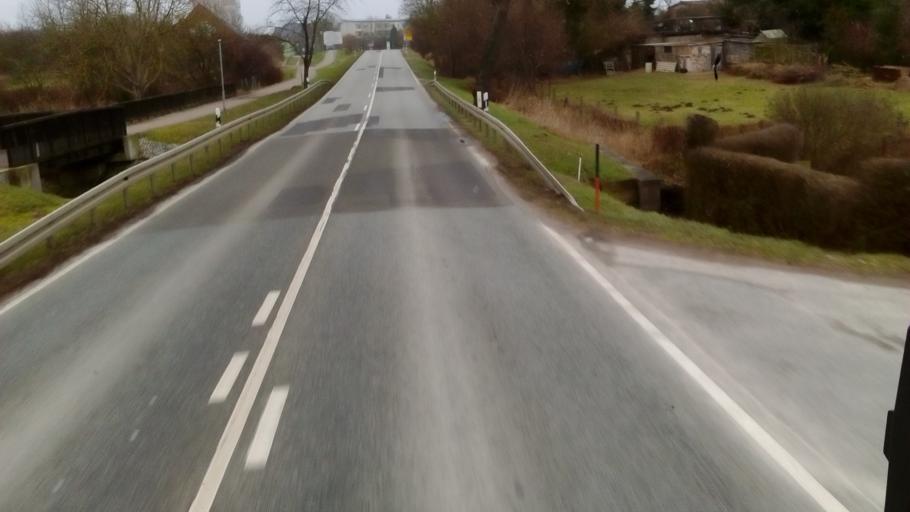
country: DE
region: Mecklenburg-Vorpommern
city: Strasburg
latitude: 53.5033
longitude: 13.7362
